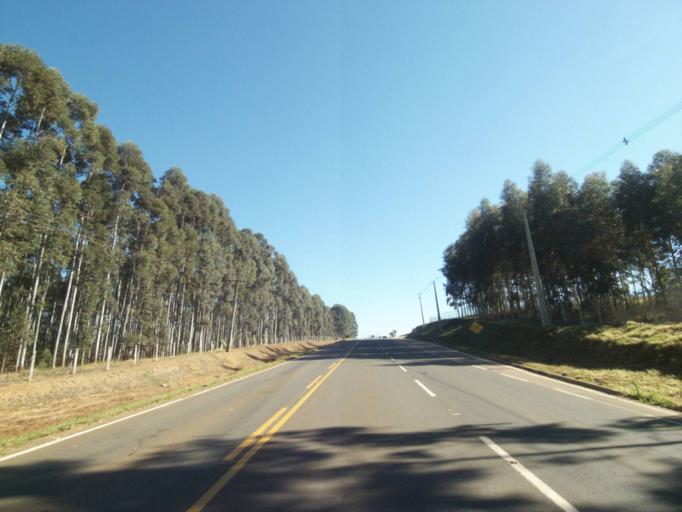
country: BR
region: Parana
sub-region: Tibagi
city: Tibagi
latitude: -24.5113
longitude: -50.4328
